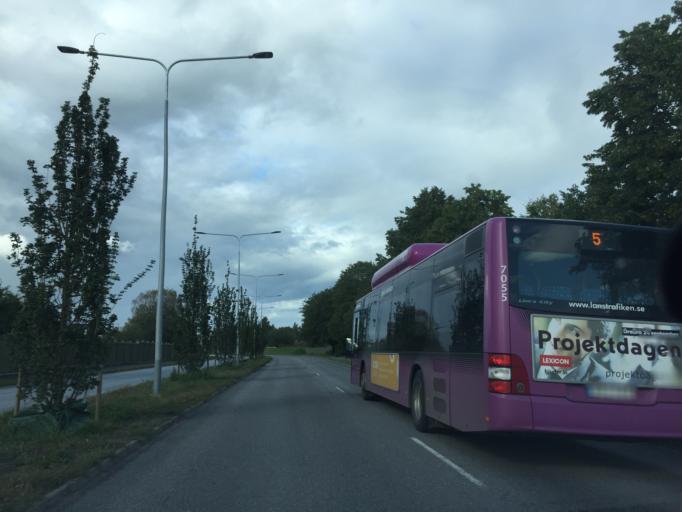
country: SE
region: OErebro
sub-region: Orebro Kommun
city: Orebro
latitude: 59.2899
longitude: 15.2243
